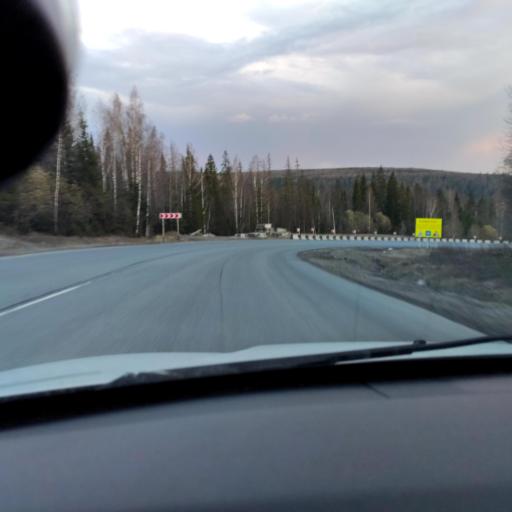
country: RU
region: Perm
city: Gremyachinsk
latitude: 58.4472
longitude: 57.8726
